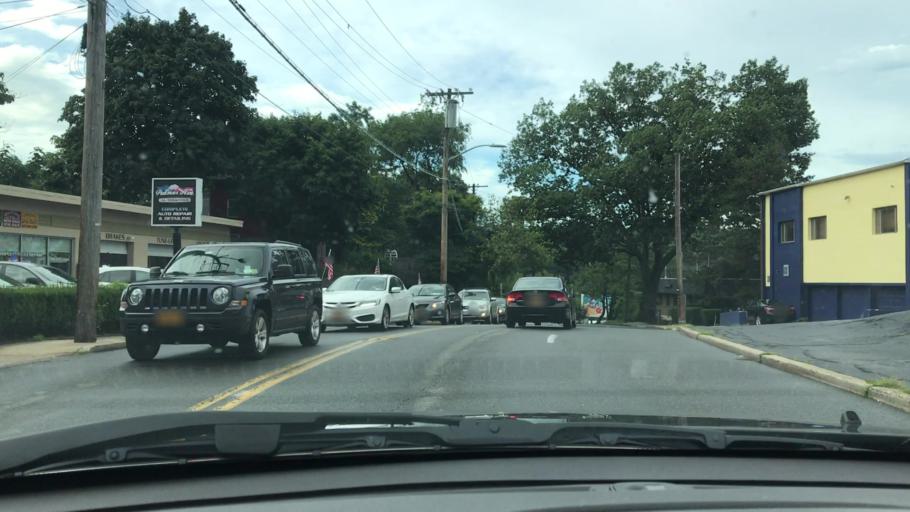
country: US
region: New York
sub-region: Westchester County
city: New Rochelle
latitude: 40.9270
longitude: -73.7730
